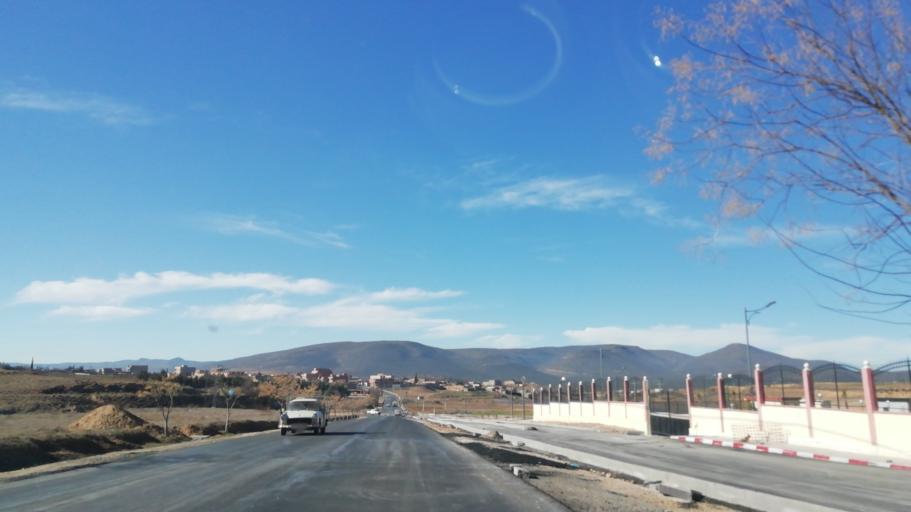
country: DZ
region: Tlemcen
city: Sebdou
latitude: 34.6557
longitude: -1.3074
